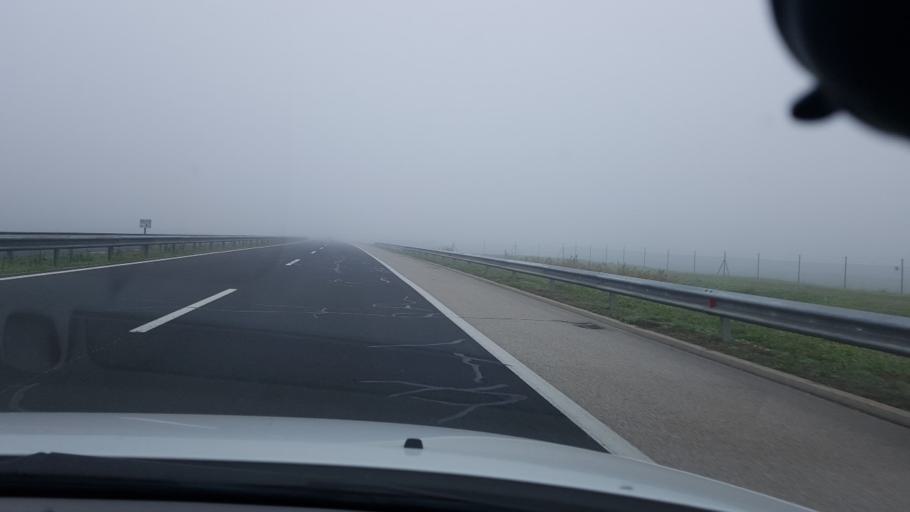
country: SI
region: Brezice
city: Brezice
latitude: 45.9000
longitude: 15.5751
